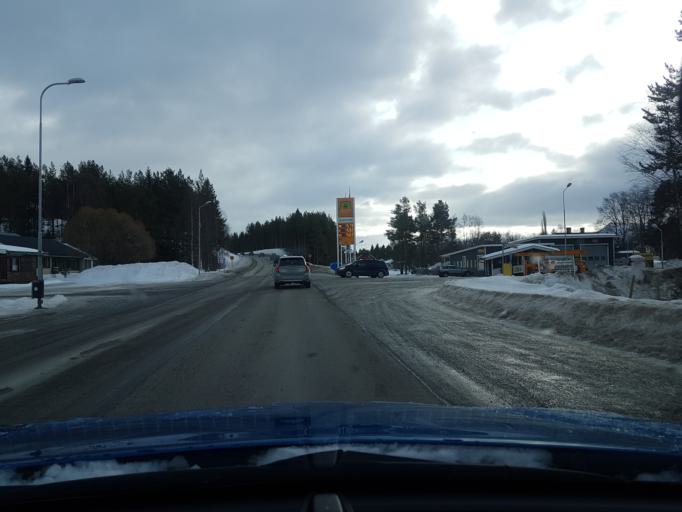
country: SE
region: Jaemtland
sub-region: Harjedalens Kommun
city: Sveg
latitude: 62.4221
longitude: 13.5364
